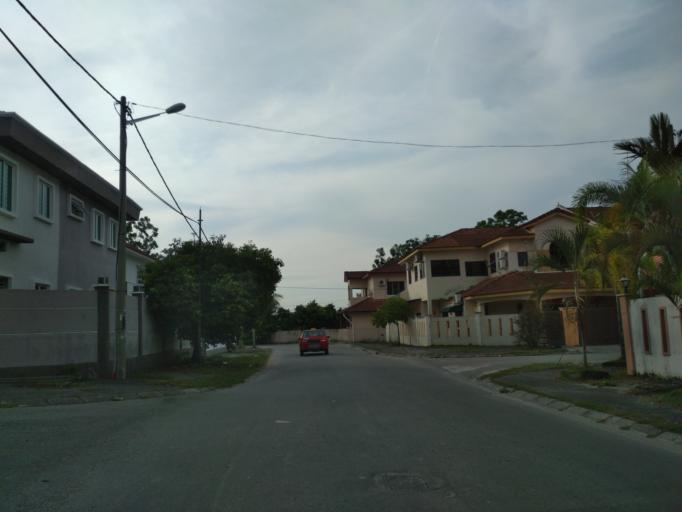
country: MY
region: Perak
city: Kampar
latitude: 4.3146
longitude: 101.1455
